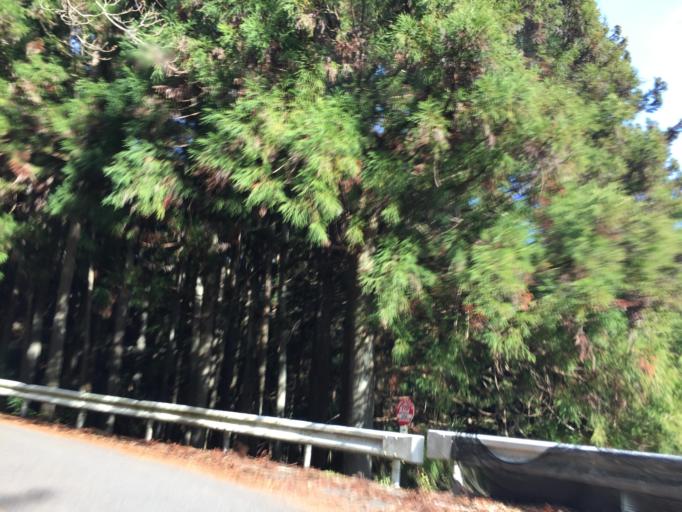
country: JP
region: Wakayama
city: Iwade
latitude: 34.1442
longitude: 135.4147
